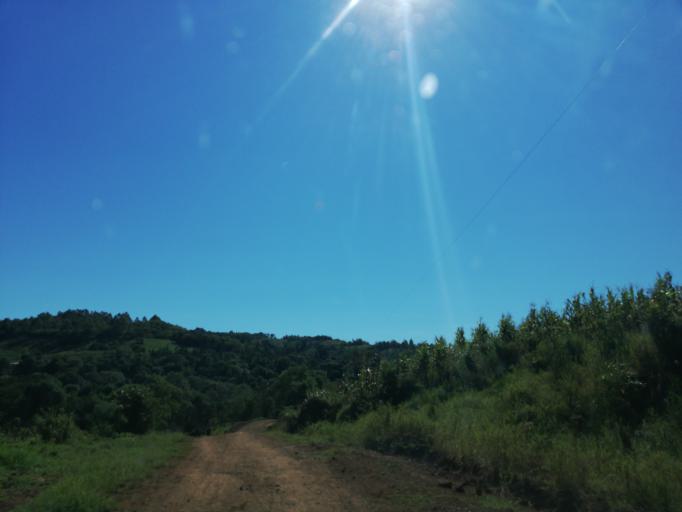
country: AR
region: Misiones
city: El Soberbio
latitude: -27.0668
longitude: -54.3867
